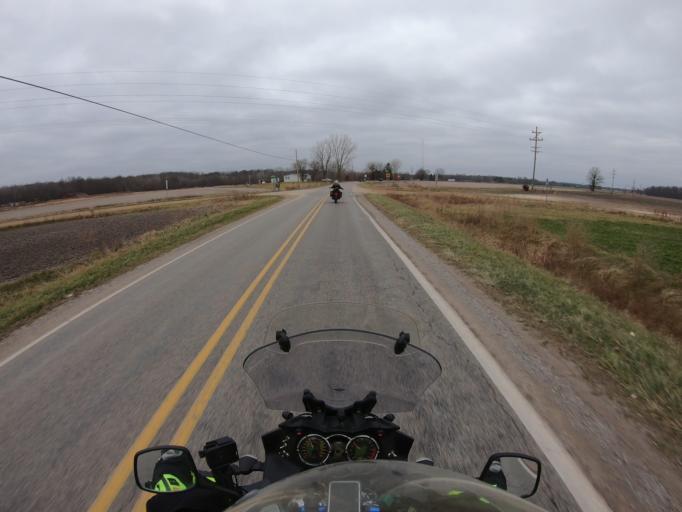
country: US
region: Michigan
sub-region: Saginaw County
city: Saint Charles
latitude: 43.2763
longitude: -84.1278
